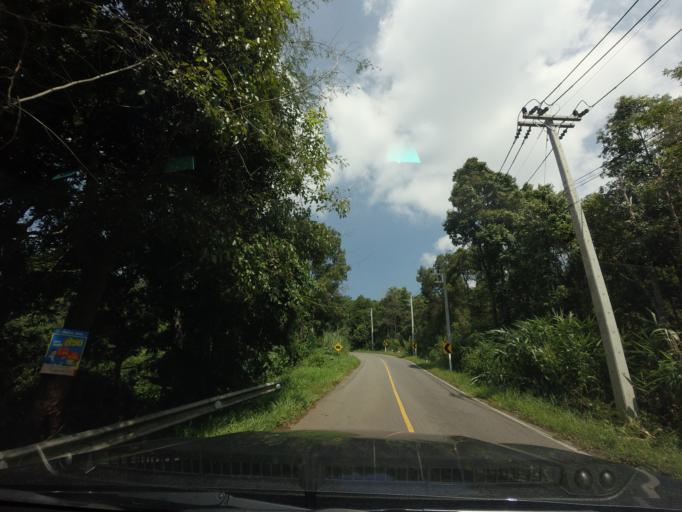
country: TH
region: Loei
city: Na Haeo
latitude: 17.4765
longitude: 100.9170
